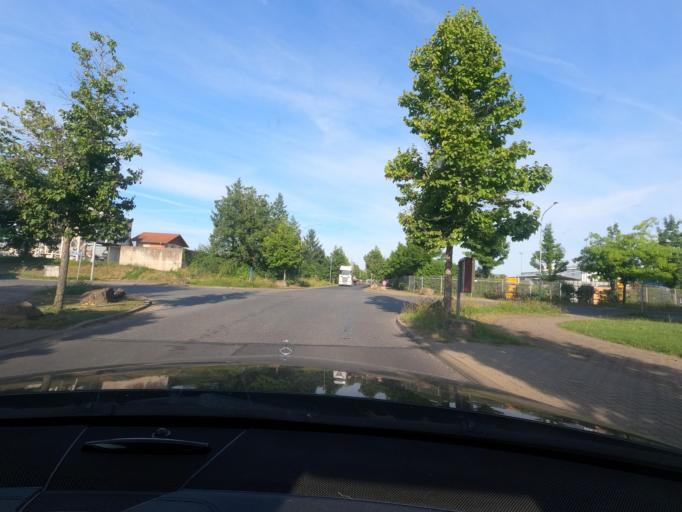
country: DE
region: Thuringia
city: Neudietendorf
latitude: 50.8806
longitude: 10.9331
